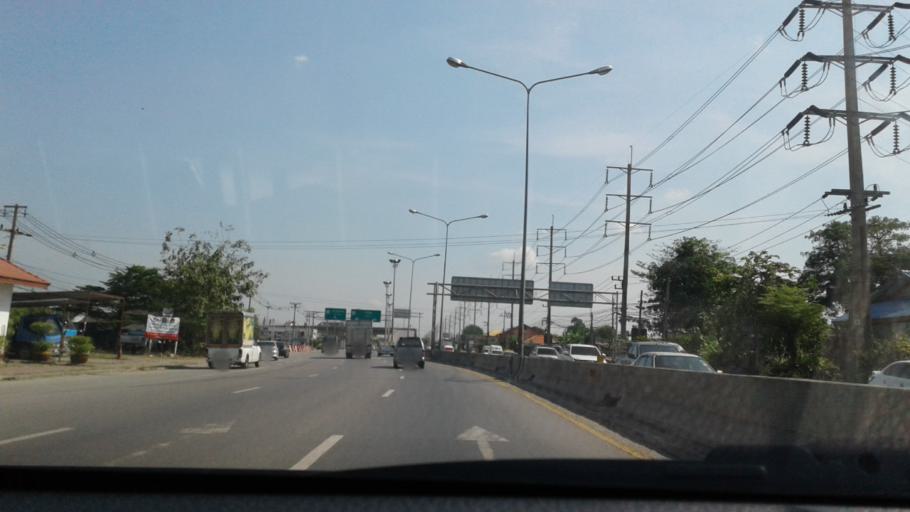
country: TH
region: Phra Nakhon Si Ayutthaya
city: Ban Bang Kadi Pathum Thani
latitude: 13.9682
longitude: 100.5510
